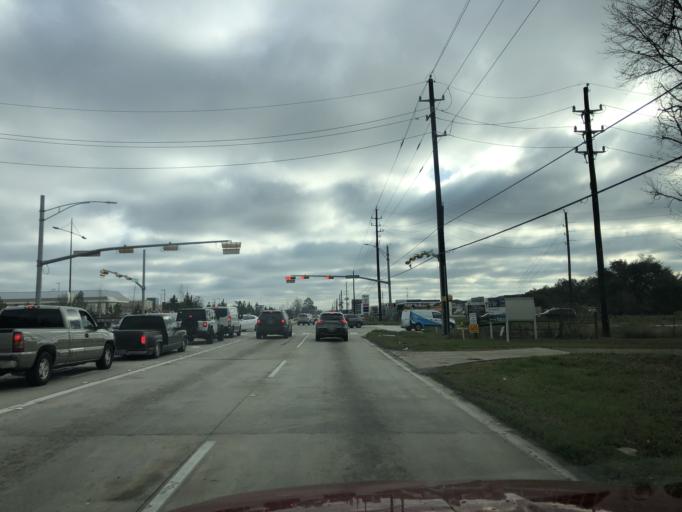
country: US
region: Texas
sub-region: Harris County
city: Spring
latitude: 30.0828
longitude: -95.4513
